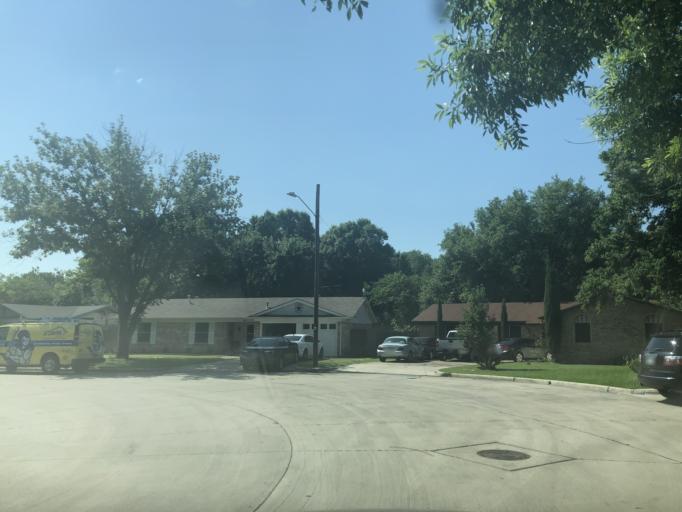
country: US
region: Texas
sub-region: Dallas County
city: Grand Prairie
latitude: 32.7241
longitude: -96.9996
